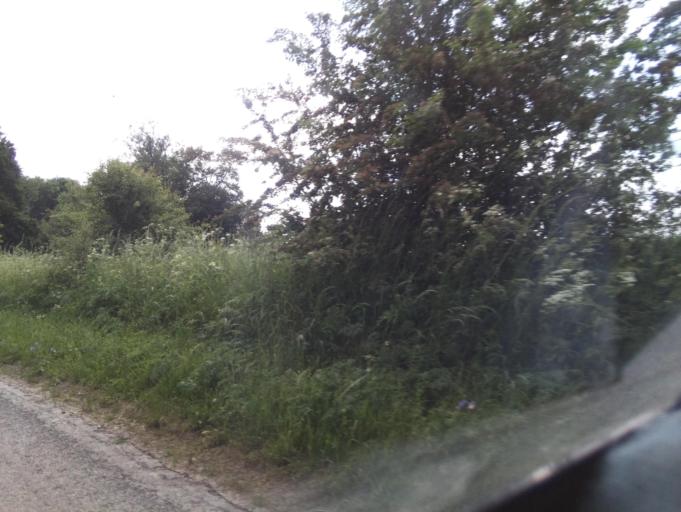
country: GB
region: England
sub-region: Wiltshire
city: Milston
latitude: 51.2600
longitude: -1.7291
